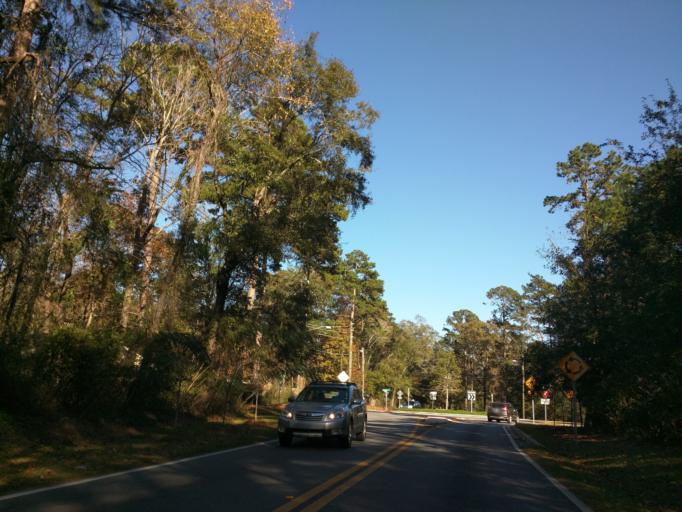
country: US
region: Florida
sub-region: Leon County
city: Tallahassee
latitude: 30.4757
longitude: -84.2203
